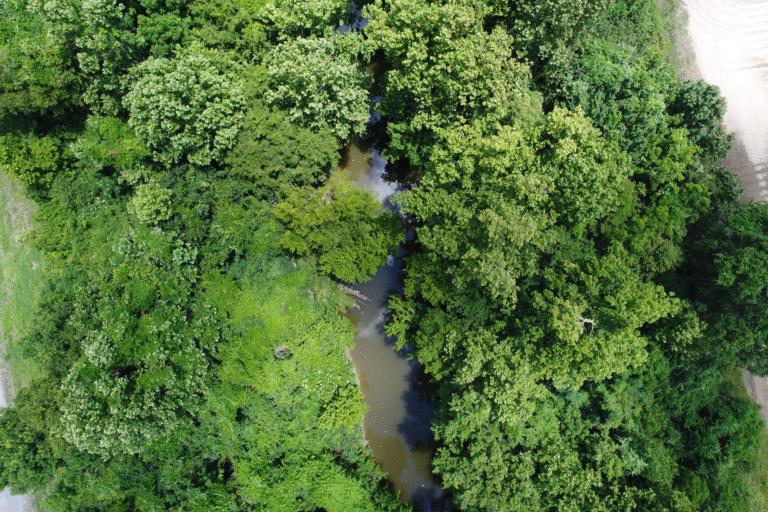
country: US
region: Mississippi
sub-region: De Soto County
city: Walls
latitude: 34.9188
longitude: -90.1592
